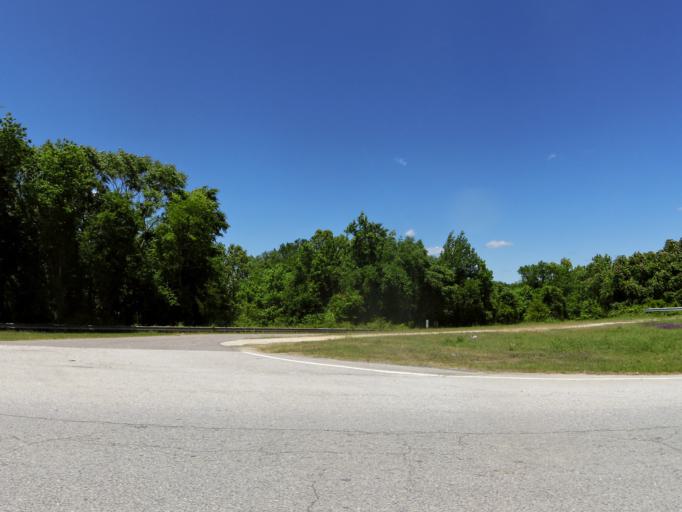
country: US
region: Georgia
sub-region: Richmond County
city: Augusta
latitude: 33.4784
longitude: -81.9554
